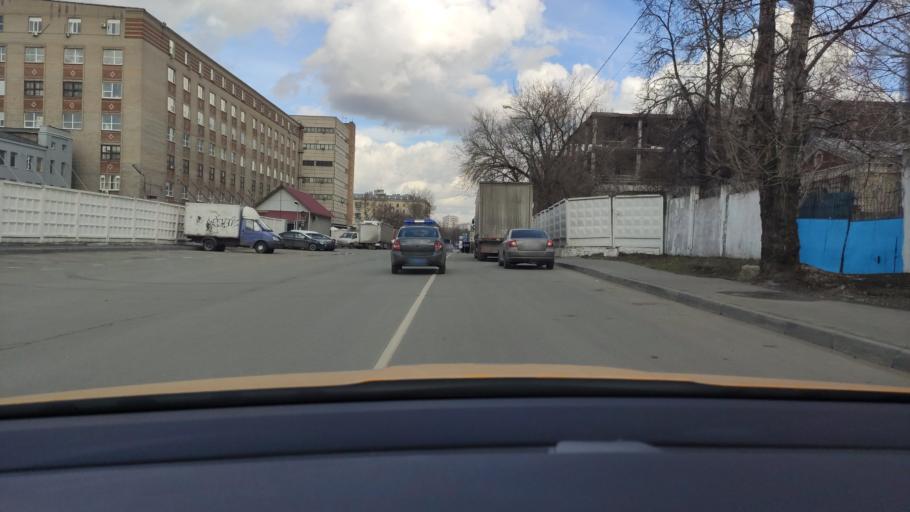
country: RU
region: Moscow
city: Ryazanskiy
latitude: 55.7206
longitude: 37.7668
